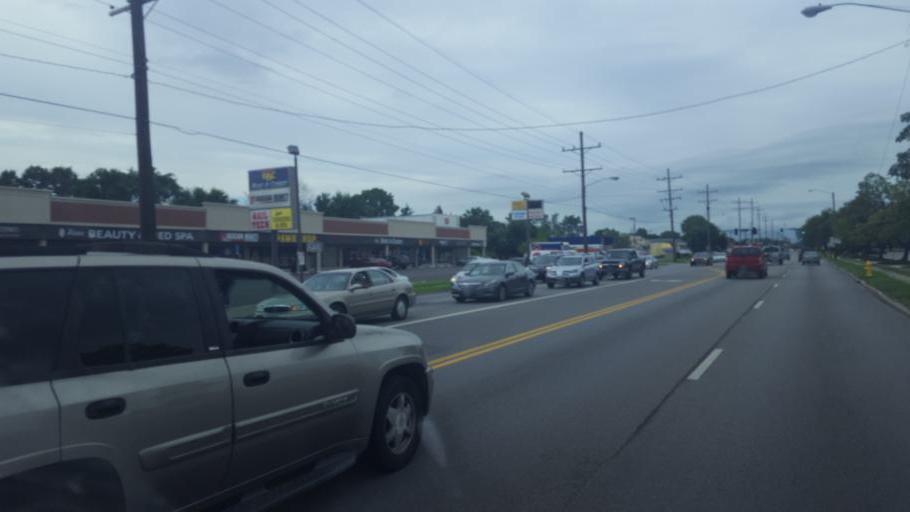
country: US
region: Ohio
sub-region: Franklin County
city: Whitehall
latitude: 39.9565
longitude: -82.8766
